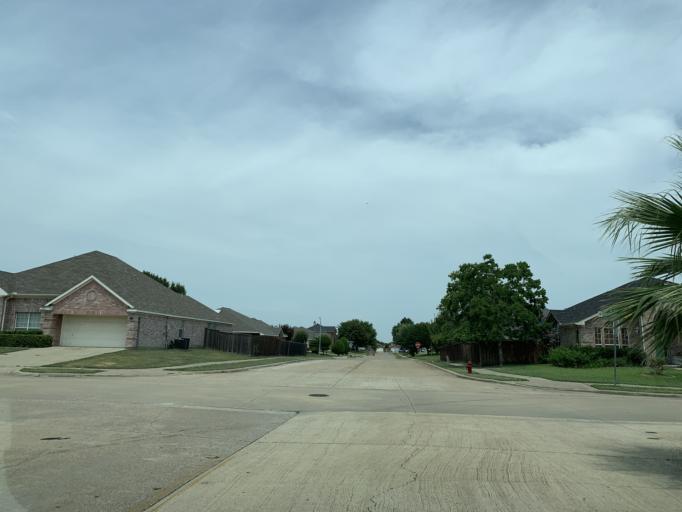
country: US
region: Texas
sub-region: Dallas County
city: Grand Prairie
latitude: 32.6610
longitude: -97.0209
